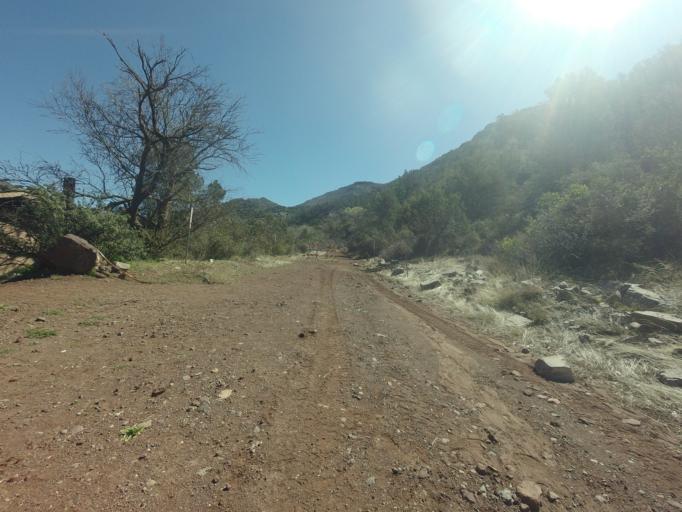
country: US
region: Arizona
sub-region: Gila County
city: Pine
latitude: 34.4049
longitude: -111.6139
